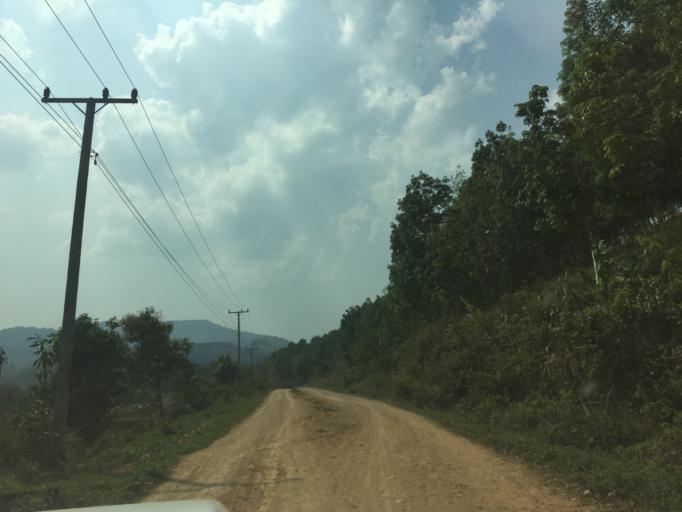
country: TH
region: Nan
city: Thung Chang
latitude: 19.7312
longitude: 100.7385
